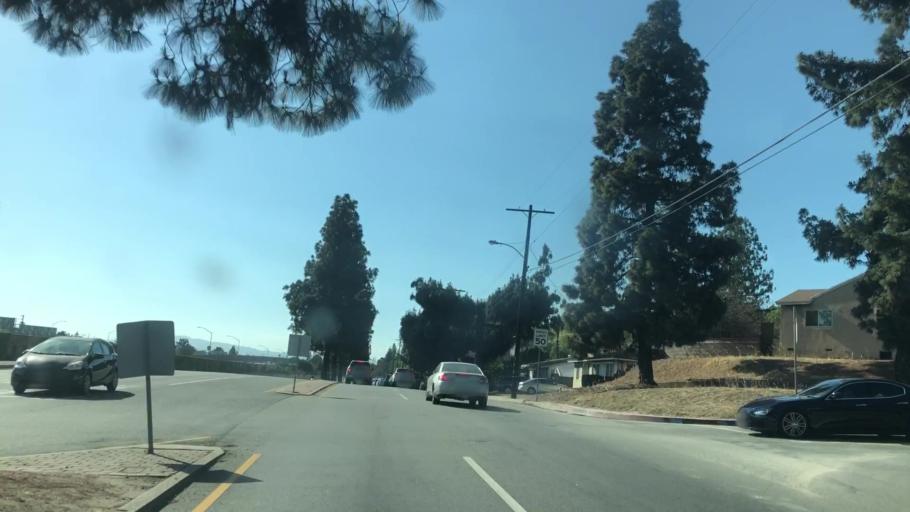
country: US
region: California
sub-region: Los Angeles County
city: North Hollywood
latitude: 34.2135
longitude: -118.3488
